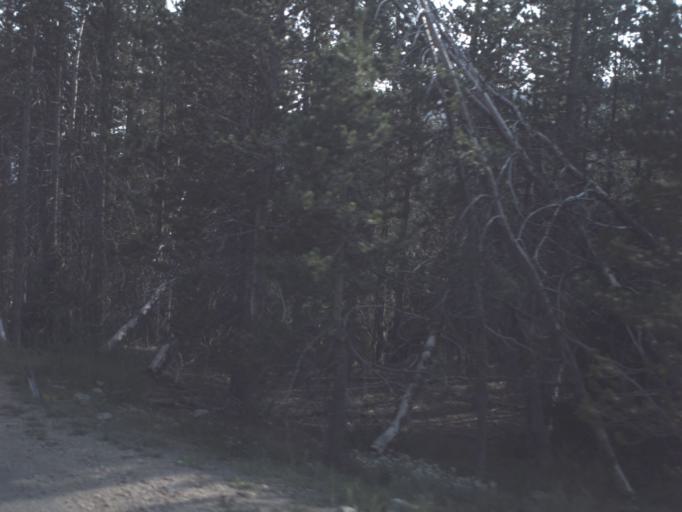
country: US
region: Utah
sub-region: Summit County
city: Kamas
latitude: 40.6585
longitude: -110.9459
